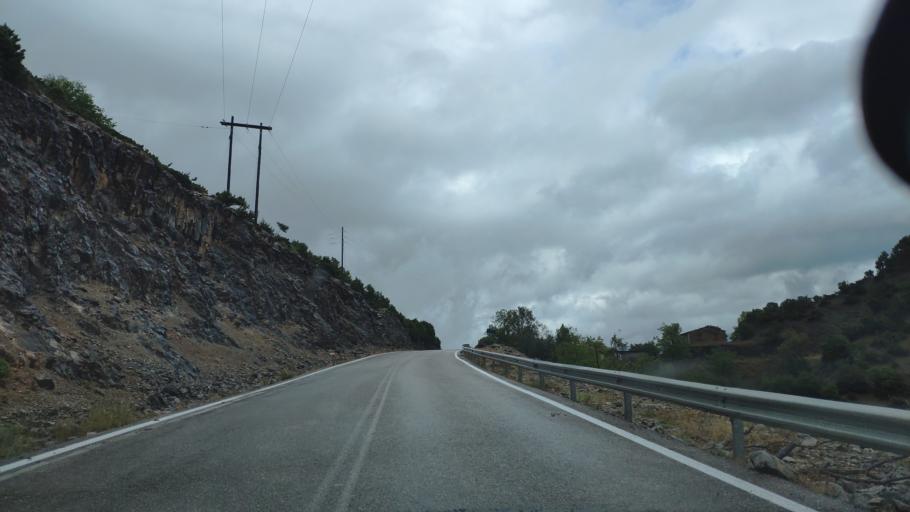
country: GR
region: Central Greece
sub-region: Nomos Evrytanias
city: Kerasochori
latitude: 39.1035
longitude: 21.4095
